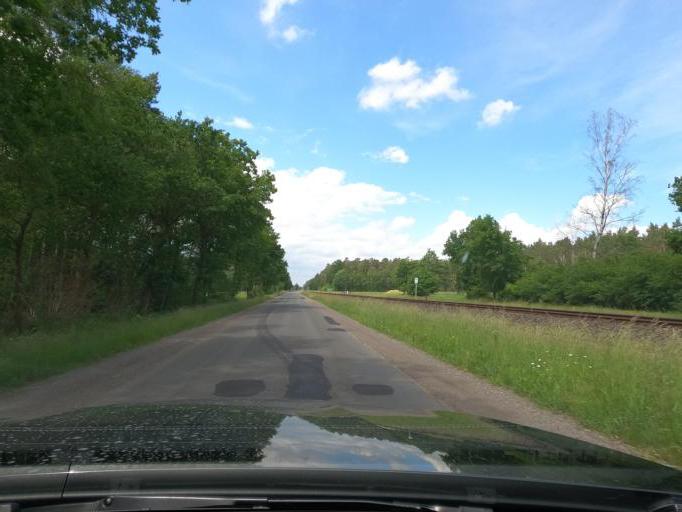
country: DE
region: Lower Saxony
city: Schwarmstedt
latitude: 52.6462
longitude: 9.6324
